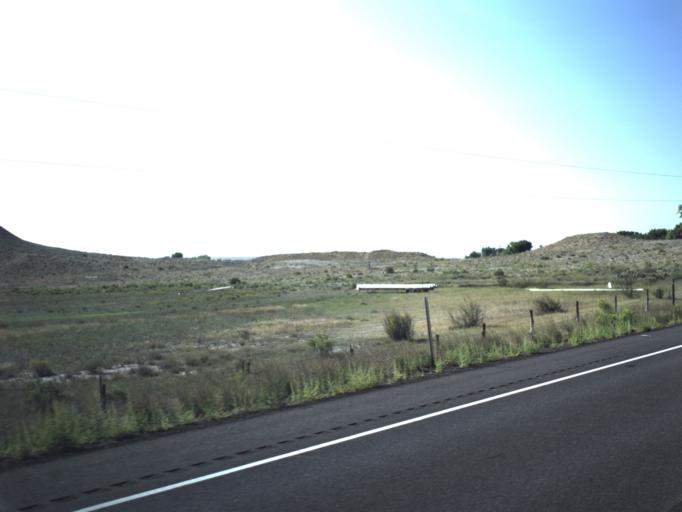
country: US
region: Utah
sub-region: Emery County
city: Huntington
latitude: 39.2707
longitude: -110.9790
